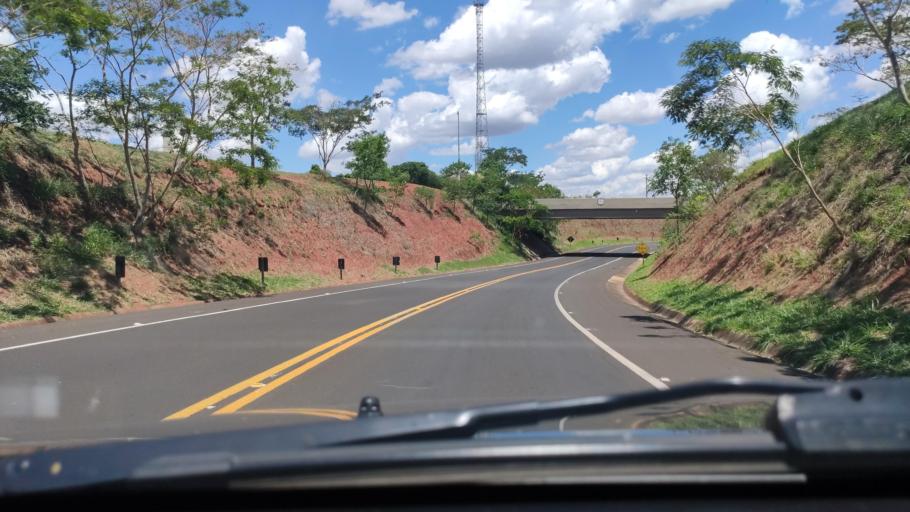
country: BR
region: Sao Paulo
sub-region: Boa Esperanca Do Sul
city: Boa Esperanca do Sul
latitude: -22.0698
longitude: -48.4324
